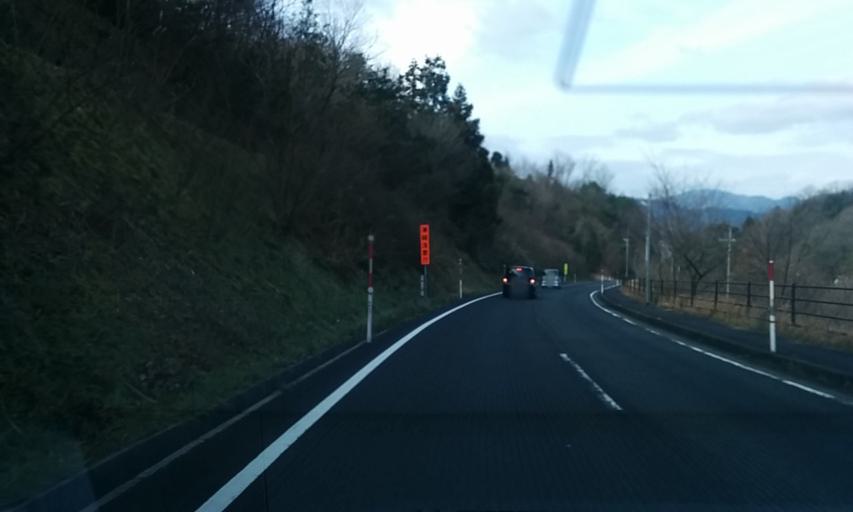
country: JP
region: Kyoto
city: Miyazu
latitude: 35.5830
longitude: 135.1127
